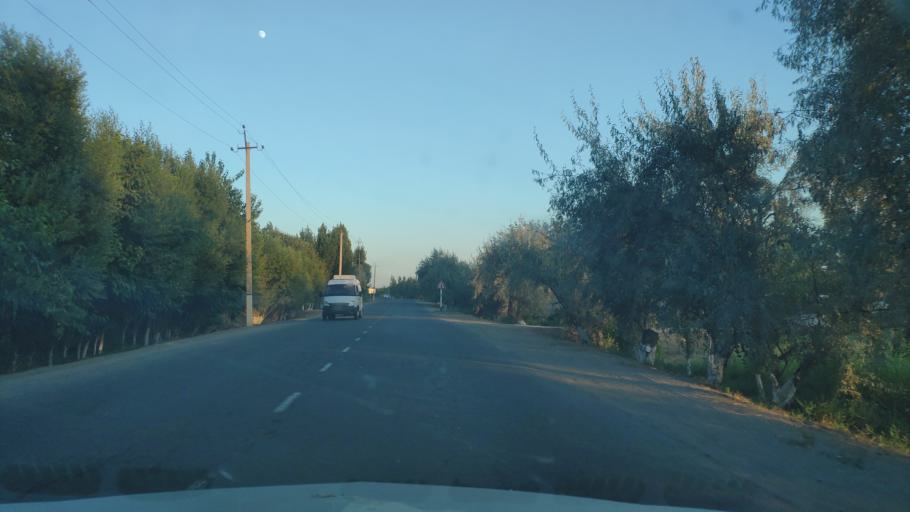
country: UZ
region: Karakalpakstan
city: To'rtko'l Shahri
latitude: 41.5634
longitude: 60.9540
